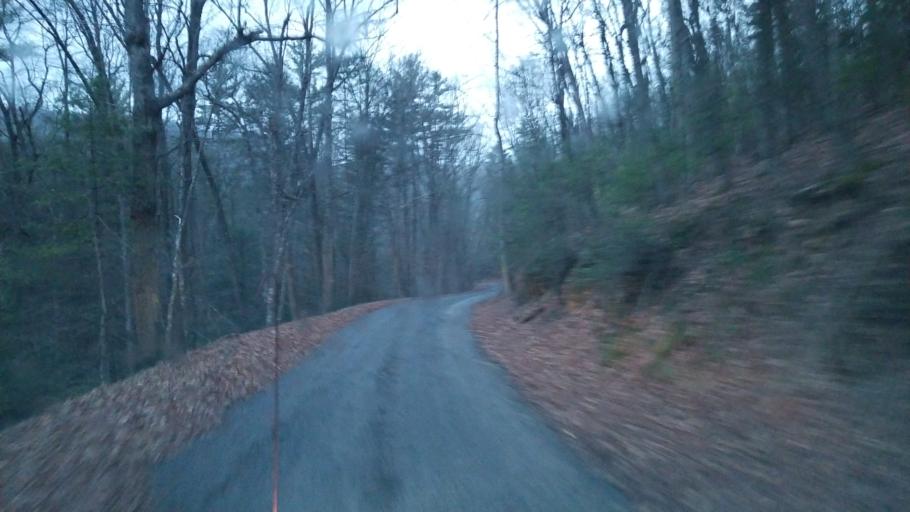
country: US
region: Virginia
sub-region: Pulaski County
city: Pulaski
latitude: 37.1136
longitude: -80.8892
